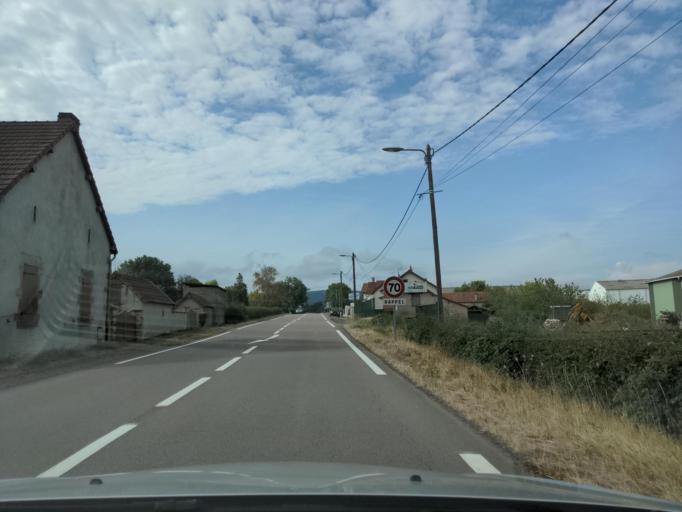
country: FR
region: Bourgogne
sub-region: Departement de Saone-et-Loire
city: Autun
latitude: 46.9791
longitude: 4.3096
